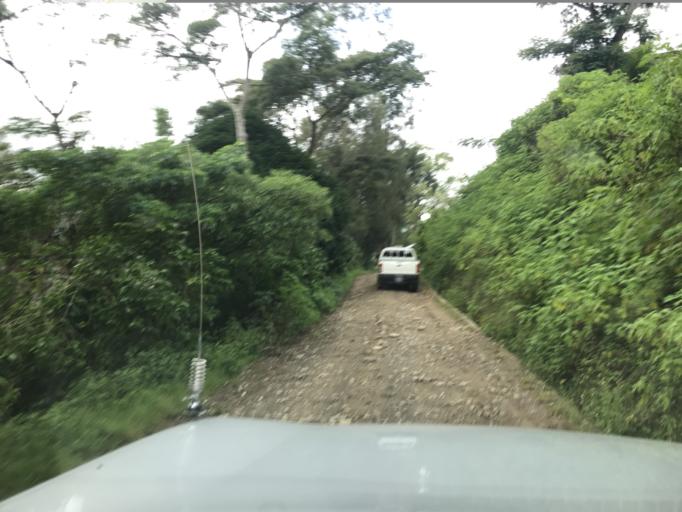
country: TL
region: Aileu
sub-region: Aileu Villa
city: Aileu
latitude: -8.8524
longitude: 125.5826
